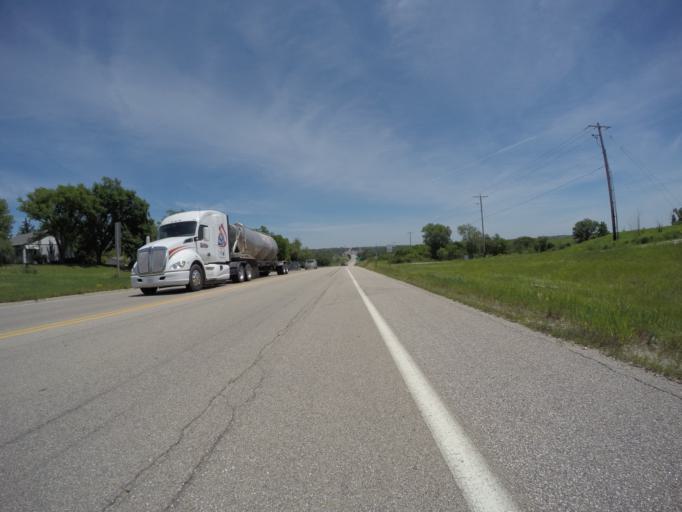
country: US
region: Kansas
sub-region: Marshall County
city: Marysville
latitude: 39.8422
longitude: -96.6696
